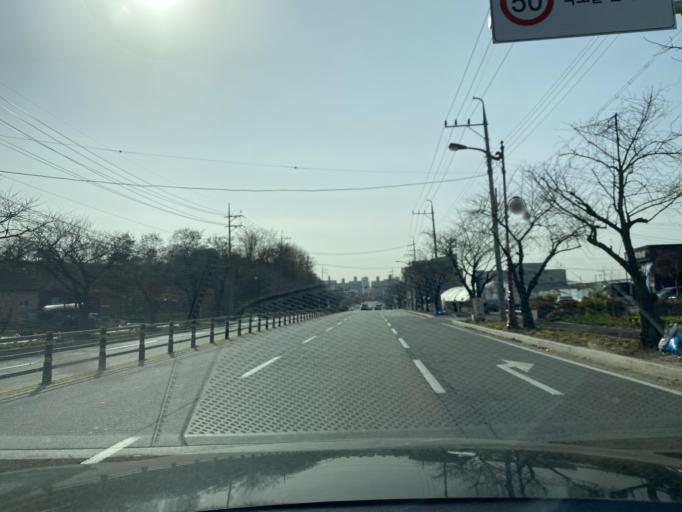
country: KR
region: Chungcheongnam-do
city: Yesan
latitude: 36.6958
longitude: 126.8369
